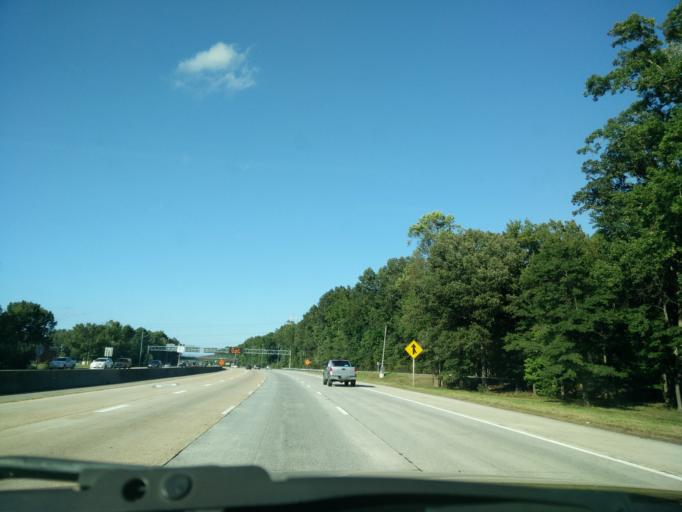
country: US
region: Virginia
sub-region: City of Chesapeake
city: Chesapeake
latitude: 36.8090
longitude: -76.1950
